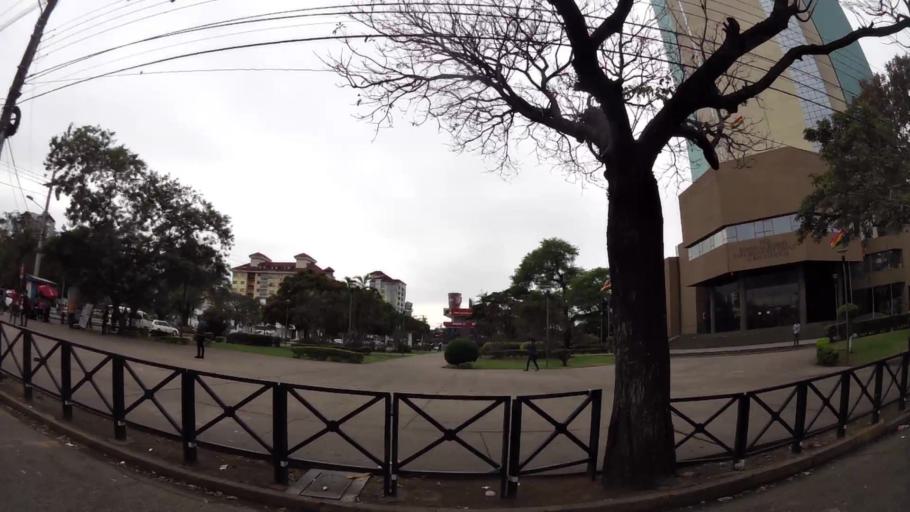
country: BO
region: Santa Cruz
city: Santa Cruz de la Sierra
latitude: -17.7747
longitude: -63.1818
